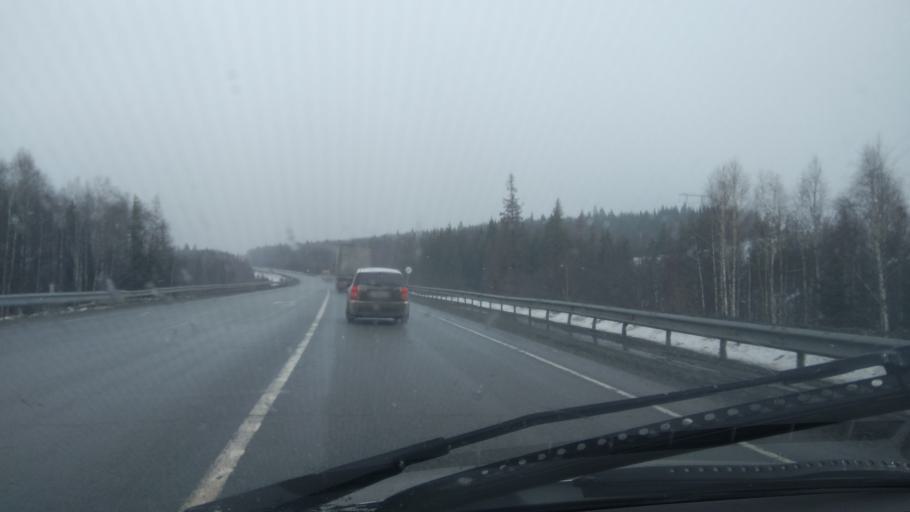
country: RU
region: Sverdlovsk
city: Arti
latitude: 56.7887
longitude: 58.5729
